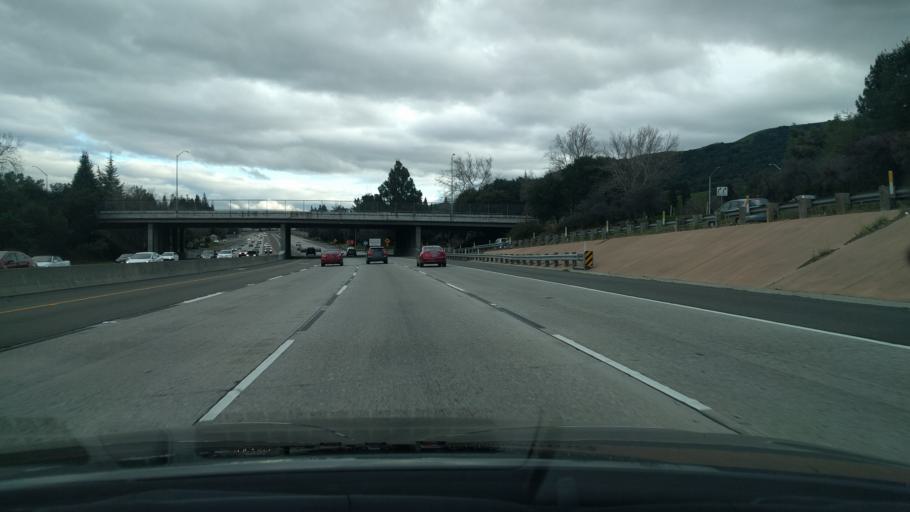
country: US
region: California
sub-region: Contra Costa County
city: Danville
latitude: 37.8126
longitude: -121.9933
